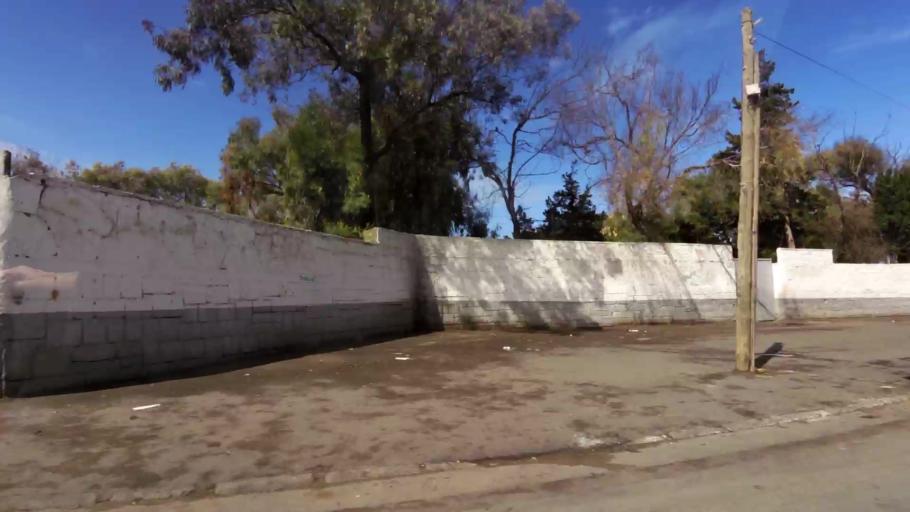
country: MA
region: Grand Casablanca
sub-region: Casablanca
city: Casablanca
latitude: 33.5694
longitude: -7.6781
